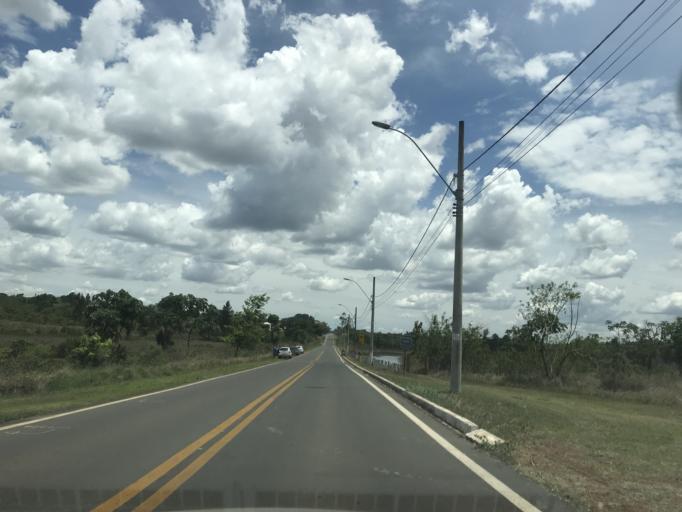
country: BR
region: Federal District
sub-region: Brasilia
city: Brasilia
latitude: -15.8962
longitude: -47.9435
